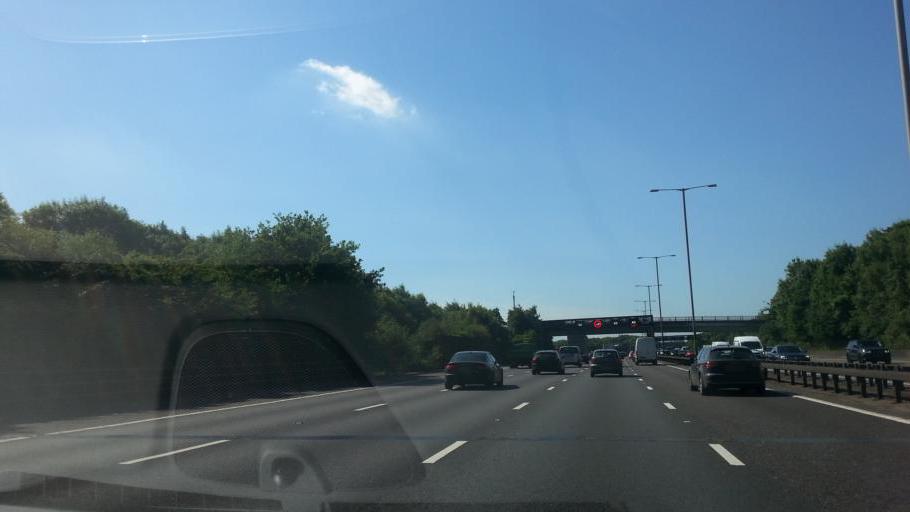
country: GB
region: England
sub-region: Greater London
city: Uxbridge
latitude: 51.5306
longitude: -0.4989
